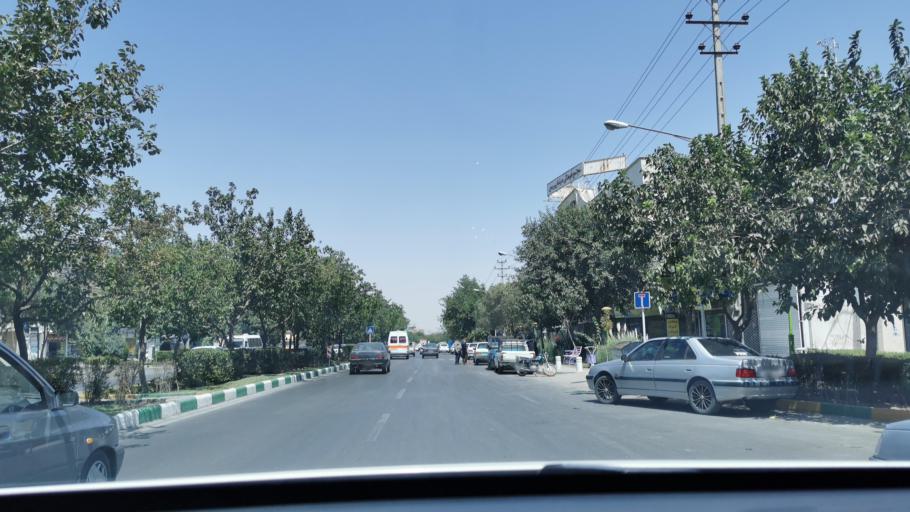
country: IR
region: Razavi Khorasan
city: Mashhad
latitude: 36.3443
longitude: 59.6260
